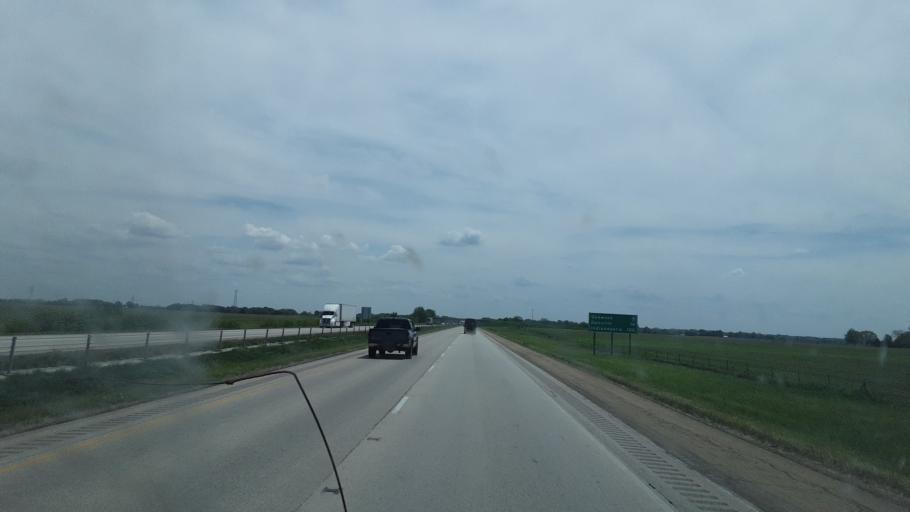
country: US
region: Illinois
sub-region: Vermilion County
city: Oakwood
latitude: 40.1237
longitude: -87.8834
